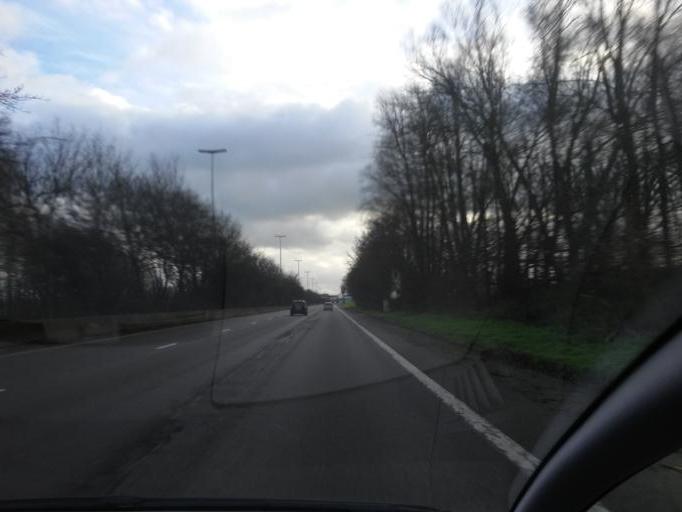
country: BE
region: Wallonia
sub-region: Province du Brabant Wallon
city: Perwez
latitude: 50.6059
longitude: 4.7832
